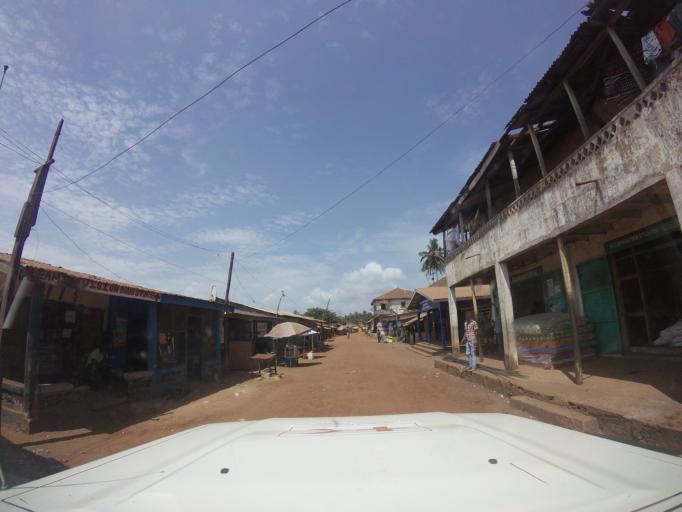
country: LR
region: Grand Cape Mount
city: Robertsport
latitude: 6.7556
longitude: -11.3616
